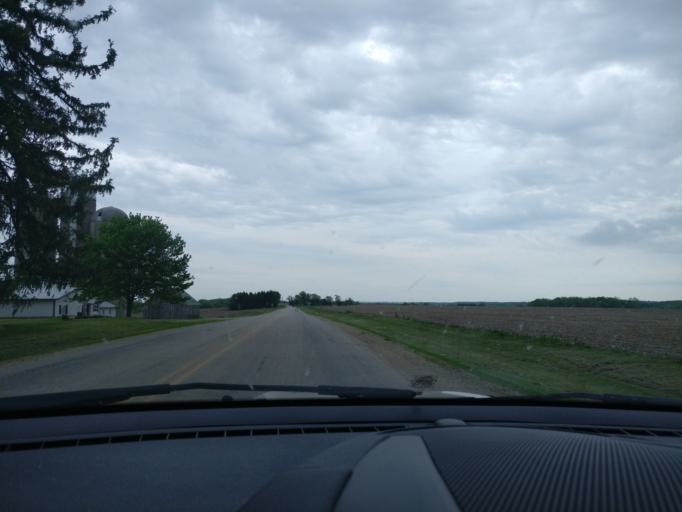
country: US
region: Wisconsin
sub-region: Lafayette County
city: Darlington
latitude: 42.7525
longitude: -90.0114
